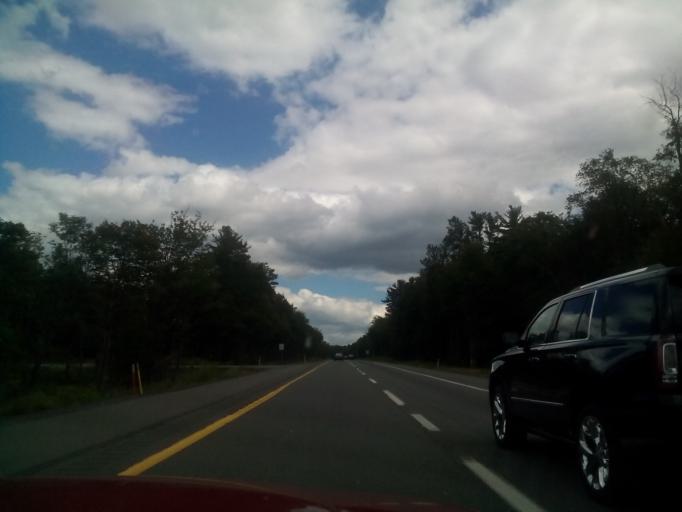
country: US
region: Pennsylvania
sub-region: Carbon County
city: Towamensing Trails
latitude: 41.0763
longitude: -75.5685
